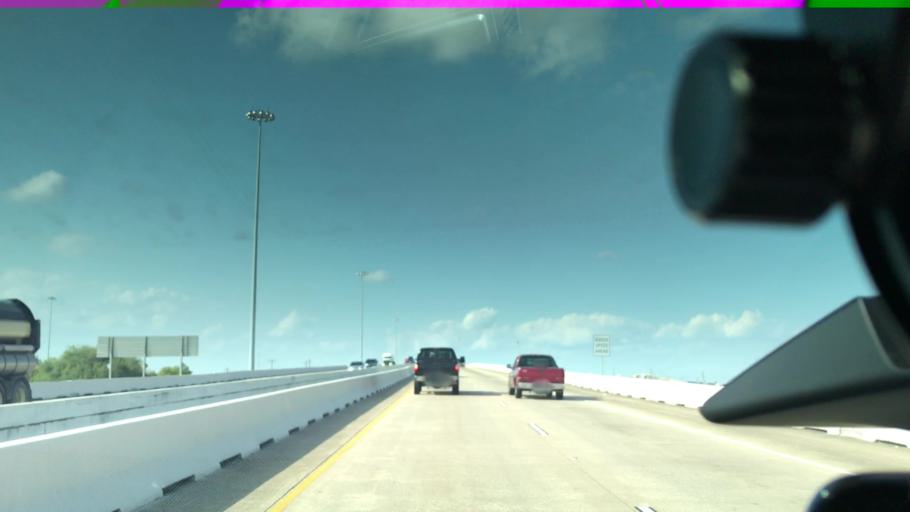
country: US
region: Texas
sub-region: Harris County
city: Deer Park
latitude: 29.7083
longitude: -95.1534
